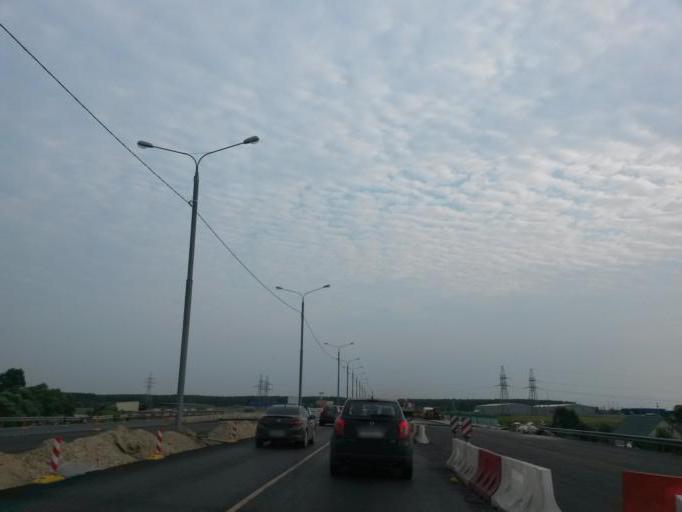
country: RU
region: Moskovskaya
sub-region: Podol'skiy Rayon
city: Podol'sk
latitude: 55.3819
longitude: 37.6050
